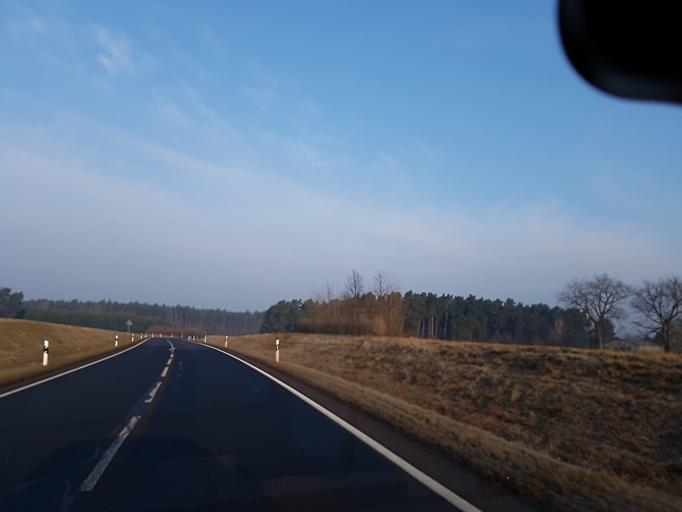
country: DE
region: Brandenburg
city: Wiesenburg
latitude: 52.0813
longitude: 12.4491
